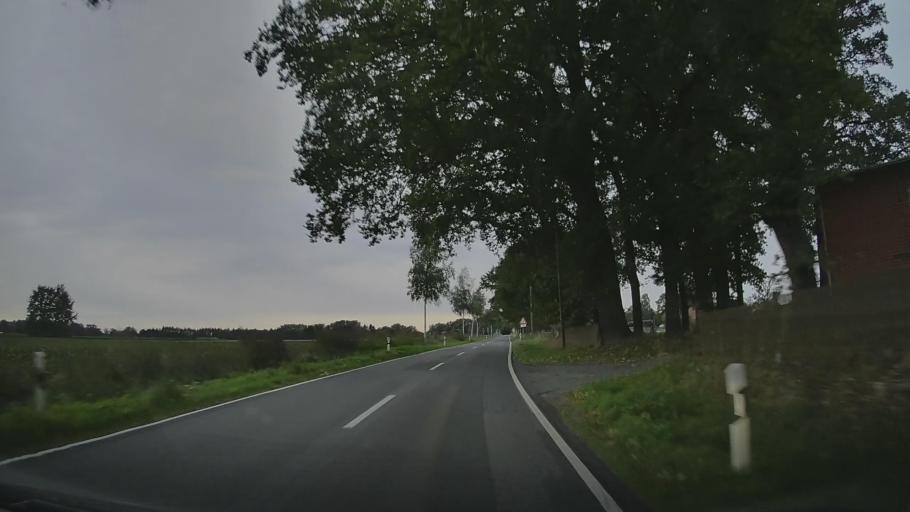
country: DE
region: Lower Saxony
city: Dunsen
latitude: 52.8918
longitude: 8.6762
